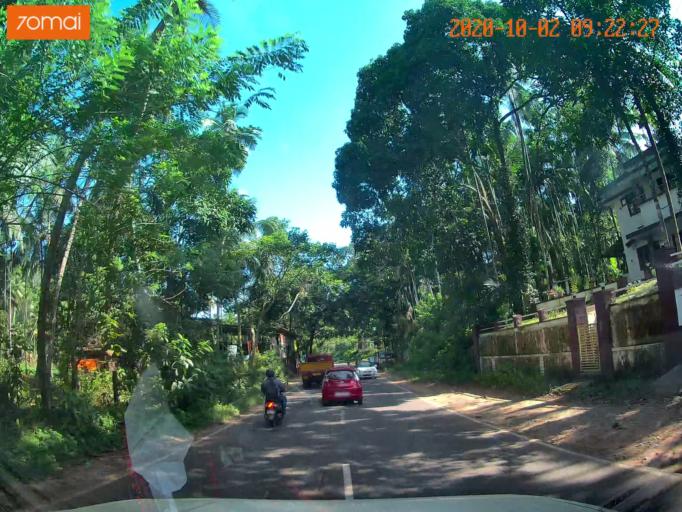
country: IN
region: Kerala
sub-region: Kozhikode
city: Naduvannur
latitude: 11.5777
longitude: 75.7563
